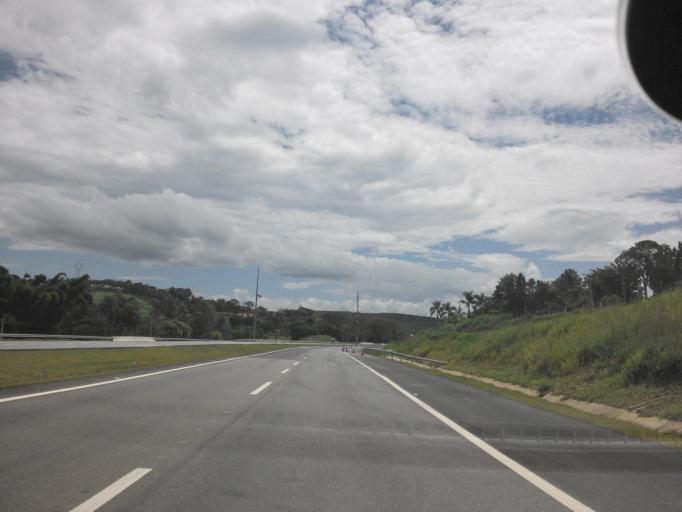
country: BR
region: Sao Paulo
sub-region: Taubate
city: Taubate
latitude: -23.0984
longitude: -45.6061
